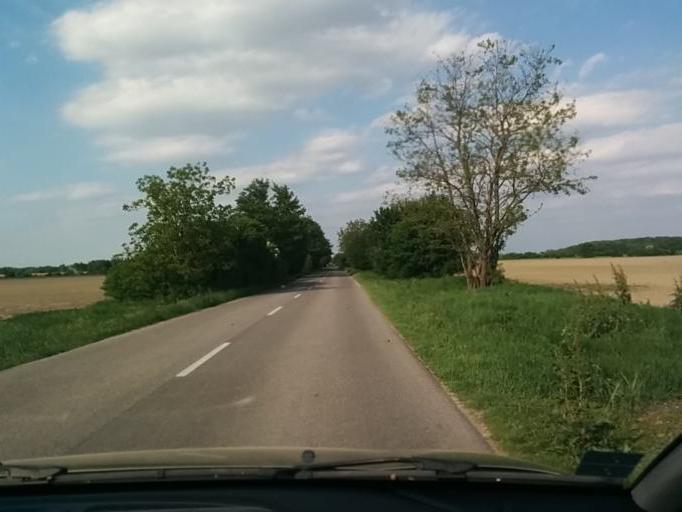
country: SK
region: Trnavsky
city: Sladkovicovo
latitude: 48.2176
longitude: 17.5531
